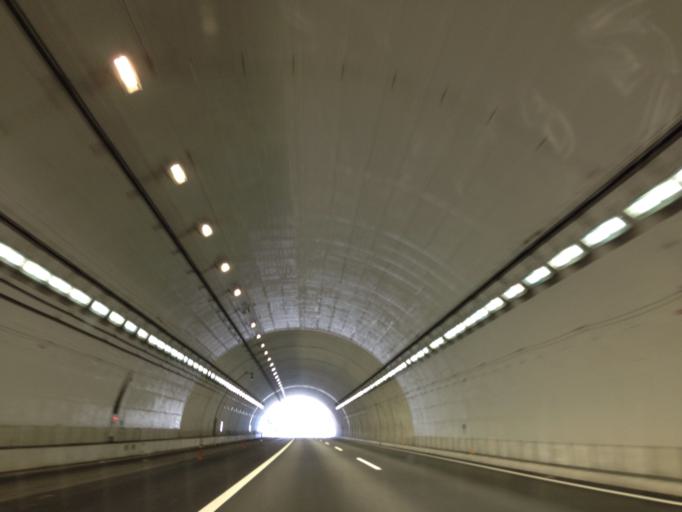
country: JP
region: Shizuoka
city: Mishima
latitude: 35.1995
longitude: 138.8883
